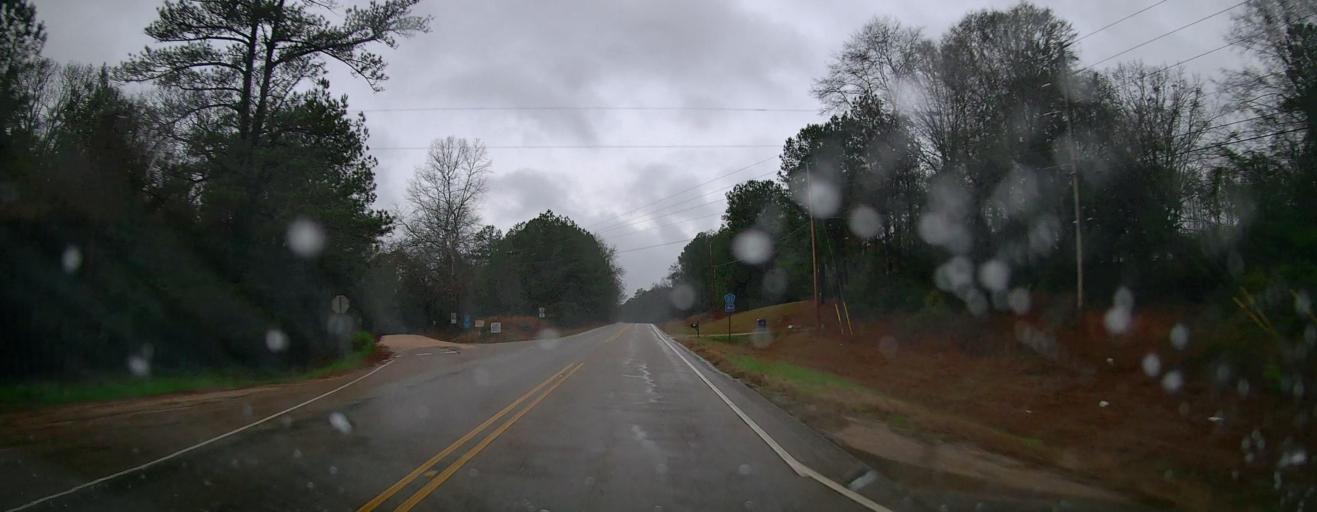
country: US
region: Alabama
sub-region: Autauga County
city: Pine Level
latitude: 32.5181
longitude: -86.6006
